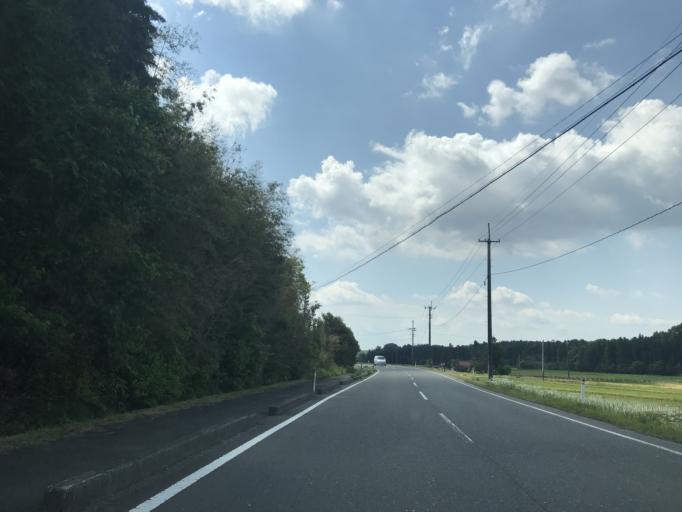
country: JP
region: Miyagi
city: Furukawa
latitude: 38.6837
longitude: 140.9746
